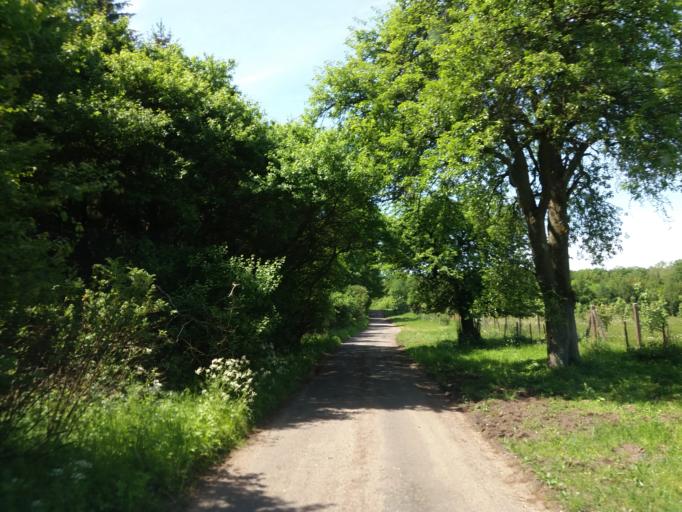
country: PL
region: West Pomeranian Voivodeship
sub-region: Powiat stargardzki
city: Dobrzany
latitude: 53.3503
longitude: 15.4774
